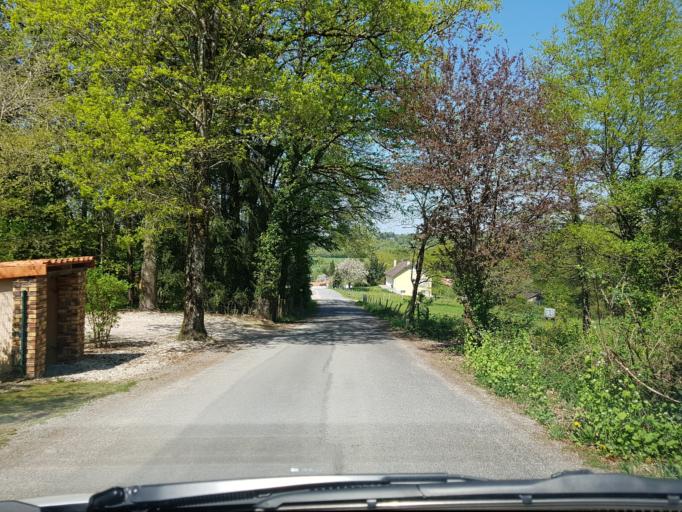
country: FR
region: Limousin
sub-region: Departement de la Haute-Vienne
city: Saint-Junien
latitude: 45.9000
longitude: 0.9073
